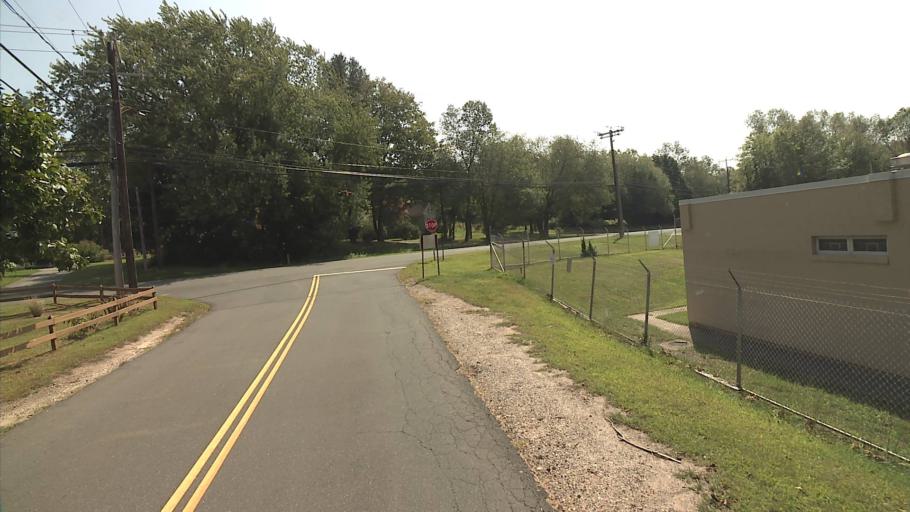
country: US
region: Connecticut
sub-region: New London County
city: Niantic
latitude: 41.3514
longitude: -72.2558
